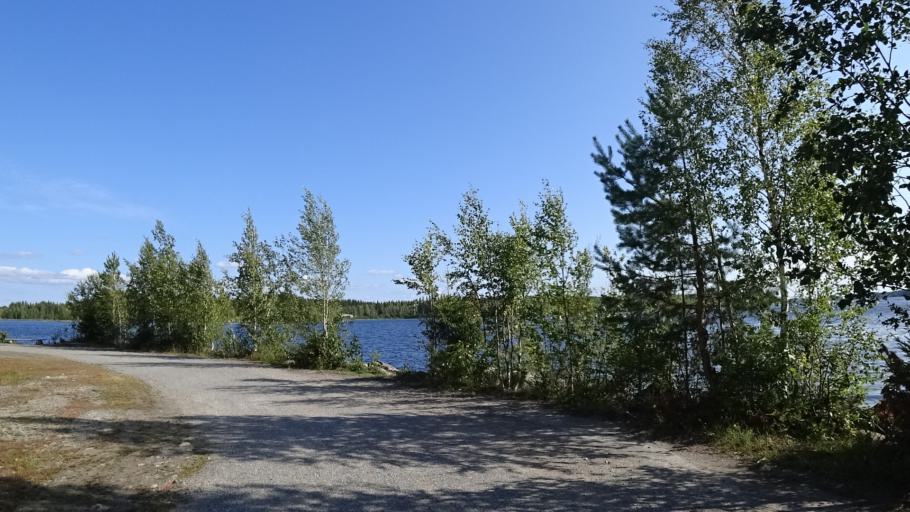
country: FI
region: North Karelia
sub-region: Joensuu
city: Eno
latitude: 62.8007
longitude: 30.1202
